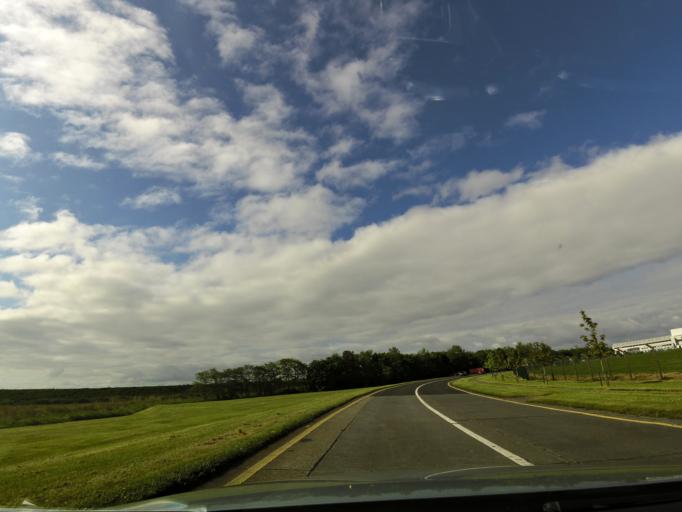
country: IE
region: Munster
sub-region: An Clar
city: Shannon
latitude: 52.6928
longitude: -8.9033
